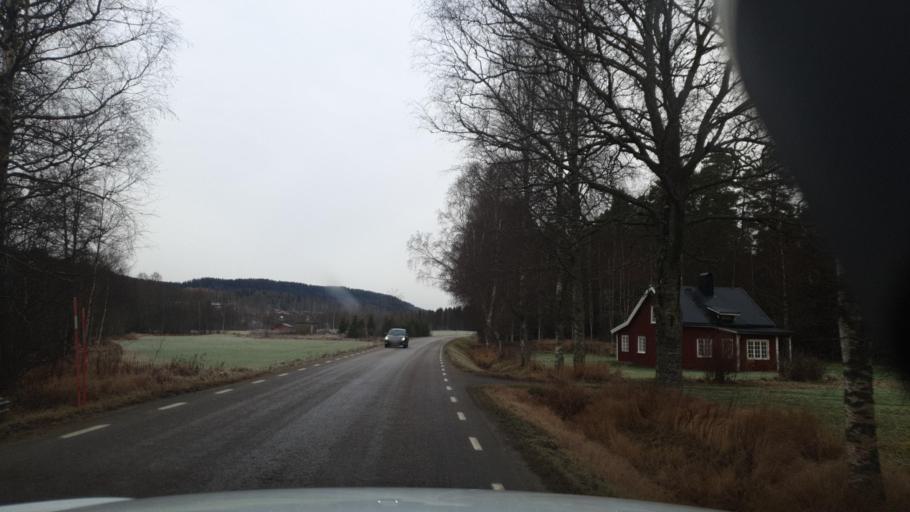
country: SE
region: Vaermland
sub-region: Arvika Kommun
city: Arvika
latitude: 59.7466
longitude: 12.8048
